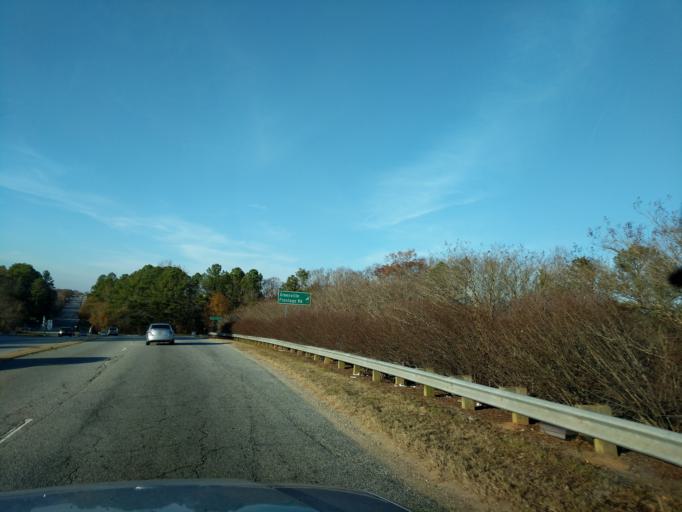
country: US
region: South Carolina
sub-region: Spartanburg County
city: Valley Falls
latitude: 34.9946
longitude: -81.9465
